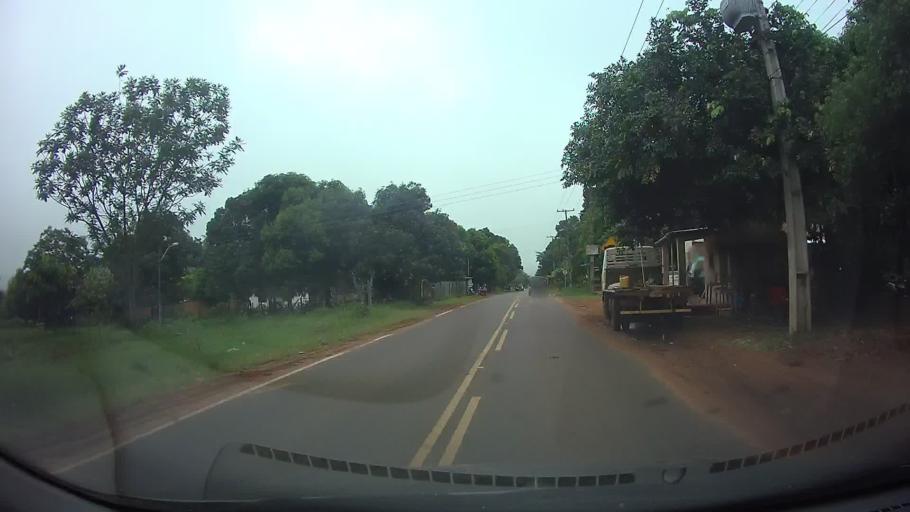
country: PY
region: Central
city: Itaugua
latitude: -25.3738
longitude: -57.3483
